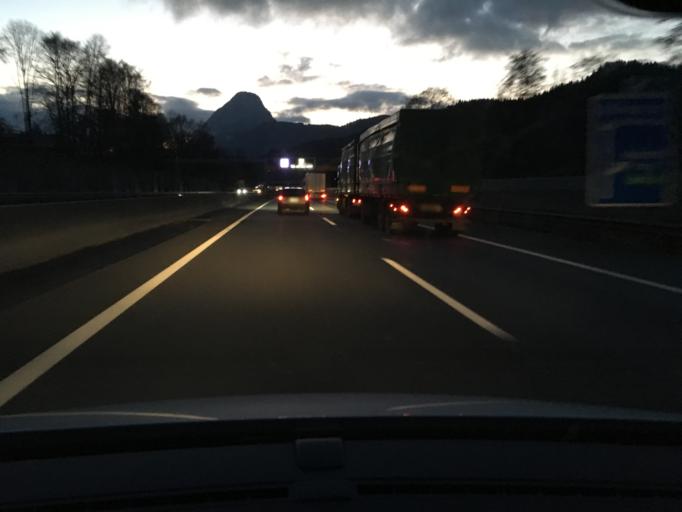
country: DE
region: Bavaria
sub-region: Upper Bavaria
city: Kiefersfelden
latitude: 47.6033
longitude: 12.1894
